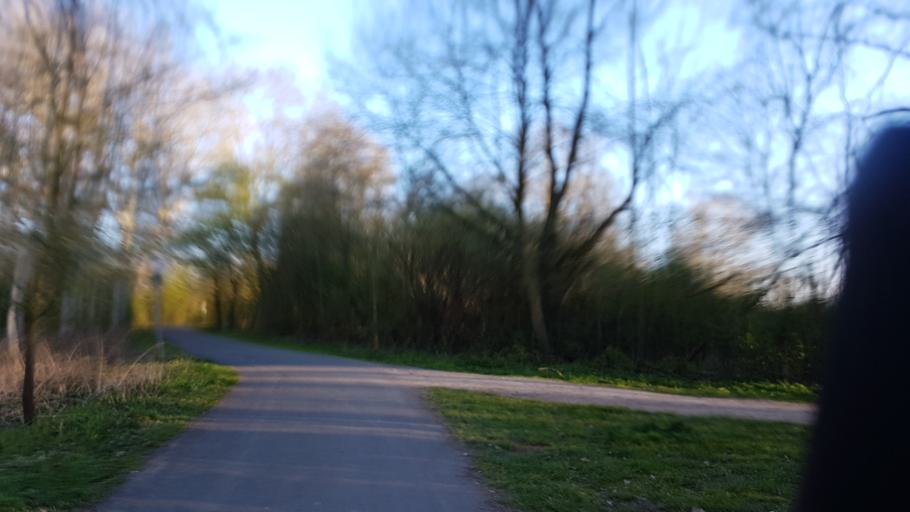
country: DE
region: Lower Saxony
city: Hemmingen
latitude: 52.3337
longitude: 9.7396
